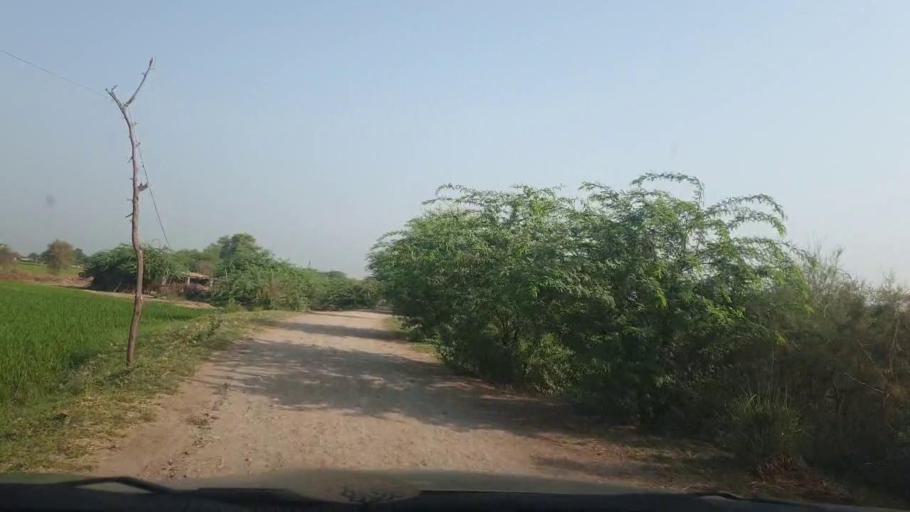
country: PK
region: Sindh
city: Larkana
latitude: 27.5959
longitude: 68.1601
